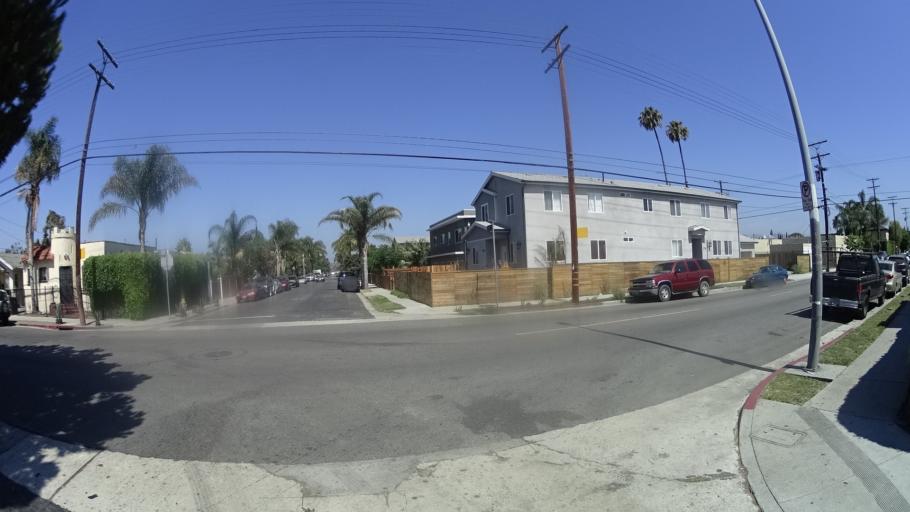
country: US
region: California
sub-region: Los Angeles County
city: Culver City
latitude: 34.0294
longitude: -118.3637
